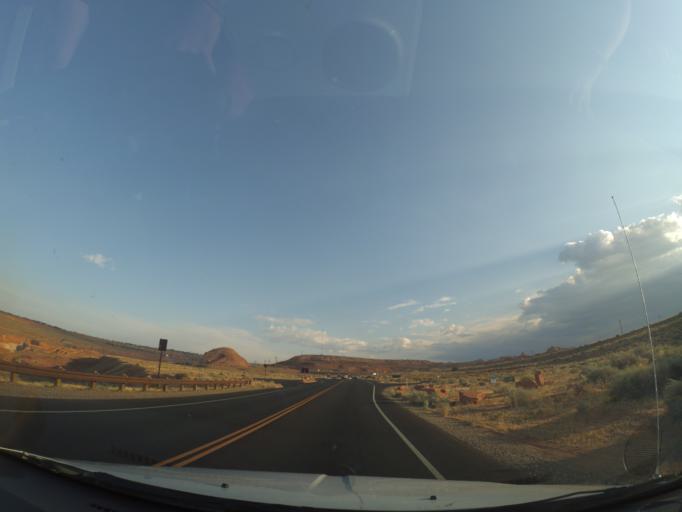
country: US
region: Arizona
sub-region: Coconino County
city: Page
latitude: 36.9447
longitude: -111.4936
